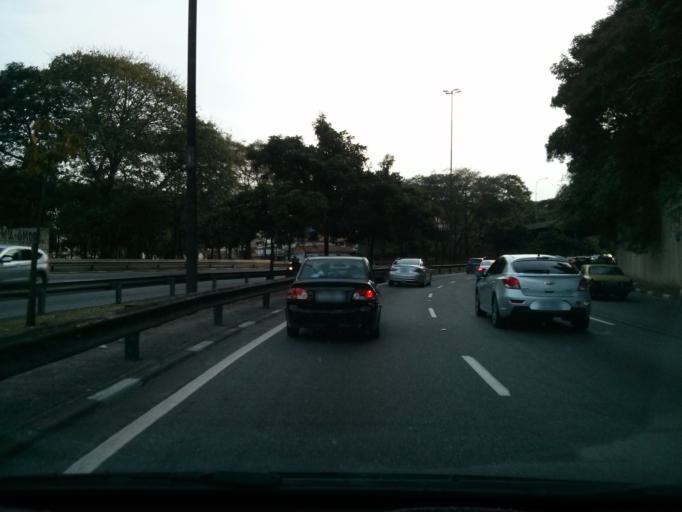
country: BR
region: Sao Paulo
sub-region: Diadema
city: Diadema
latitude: -23.6306
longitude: -46.6440
